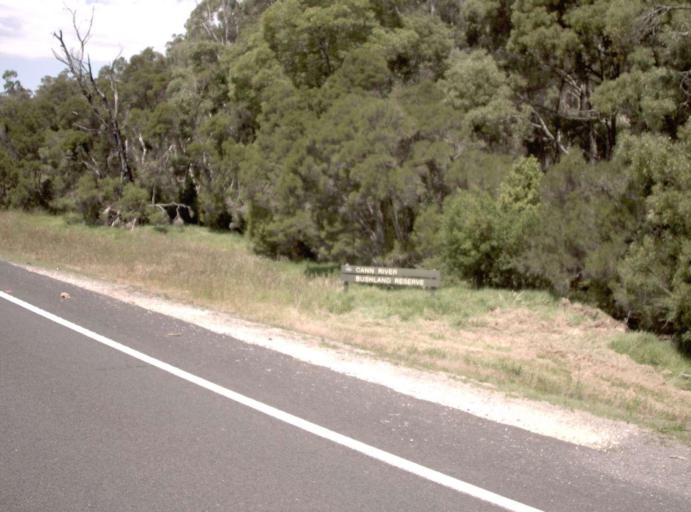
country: AU
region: New South Wales
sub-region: Bombala
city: Bombala
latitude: -37.5696
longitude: 149.1387
